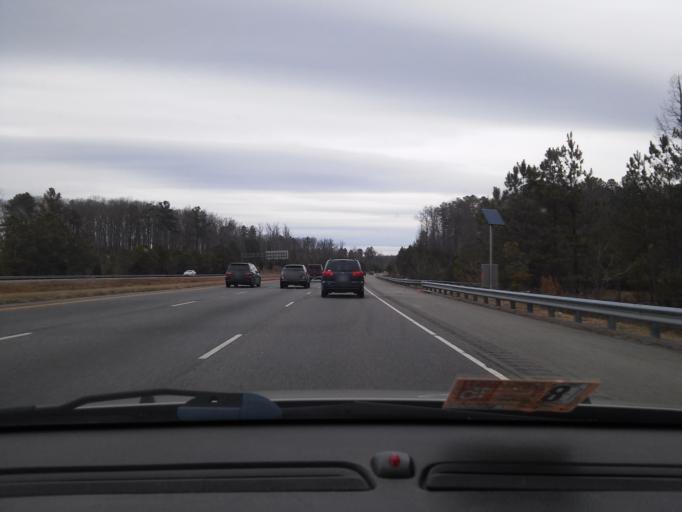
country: US
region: Virginia
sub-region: Henrico County
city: Short Pump
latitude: 37.6506
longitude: -77.6648
